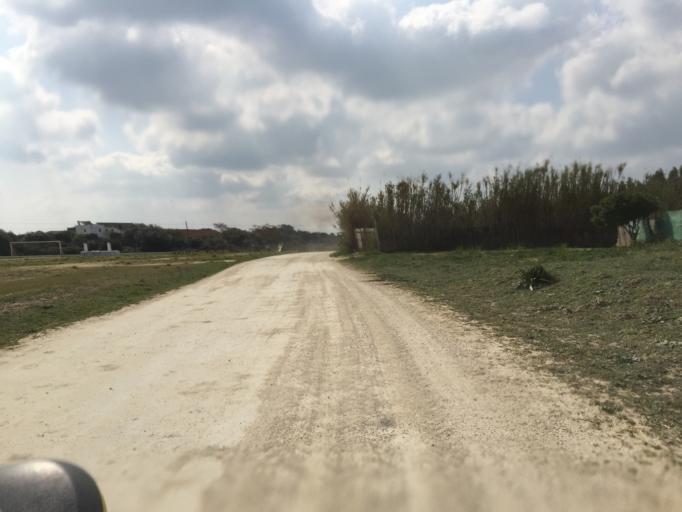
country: ES
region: Andalusia
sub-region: Provincia de Cadiz
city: Benalup-Casas Viejas
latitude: 36.3242
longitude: -5.8843
